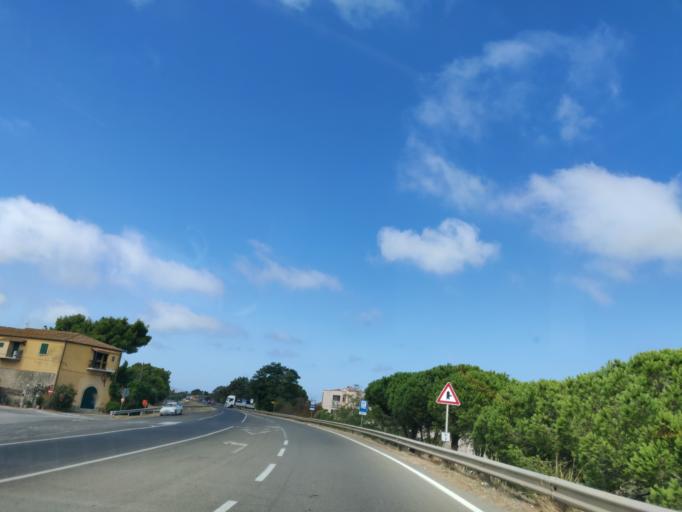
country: IT
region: Tuscany
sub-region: Provincia di Grosseto
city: Orbetello Scalo
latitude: 42.4467
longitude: 11.2512
